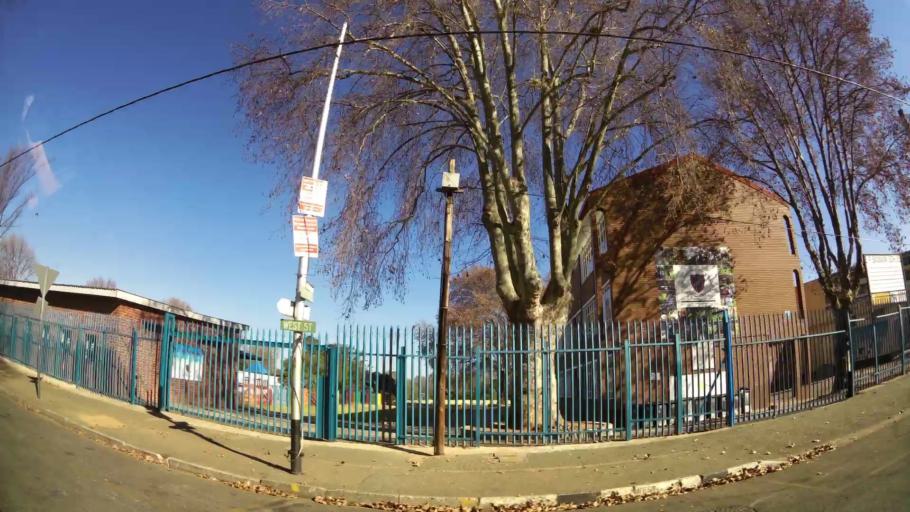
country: ZA
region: Gauteng
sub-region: City of Johannesburg Metropolitan Municipality
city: Johannesburg
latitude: -26.1984
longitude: 28.0063
